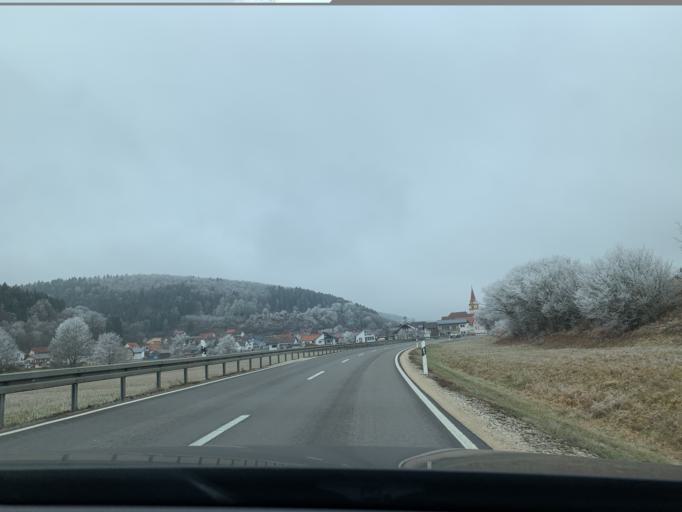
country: DE
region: Baden-Wuerttemberg
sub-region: Freiburg Region
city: Geisingen
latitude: 47.8831
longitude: 8.6552
